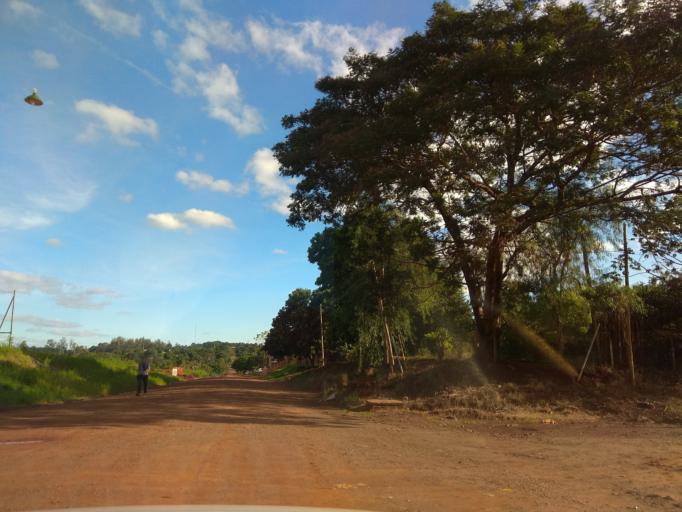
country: AR
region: Misiones
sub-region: Departamento de Capital
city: Posadas
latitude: -27.3914
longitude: -55.9275
